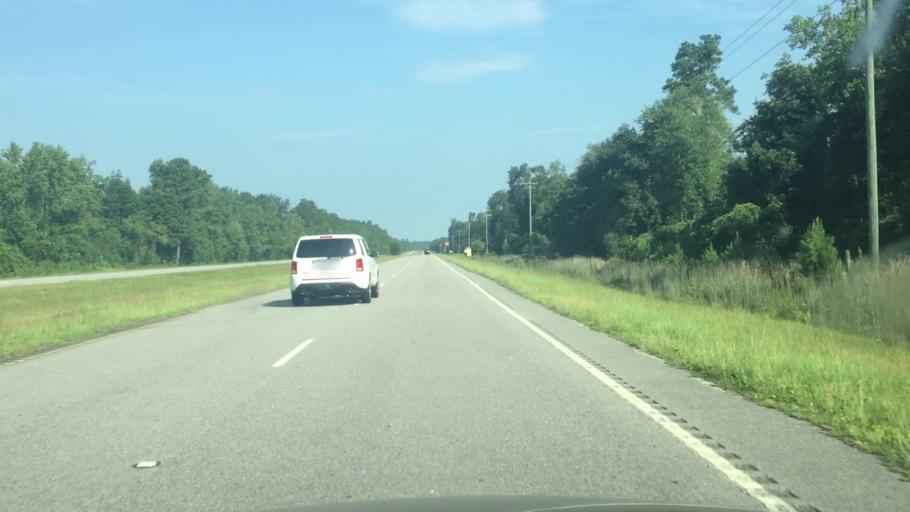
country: US
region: South Carolina
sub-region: Horry County
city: Loris
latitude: 34.0525
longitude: -78.8391
